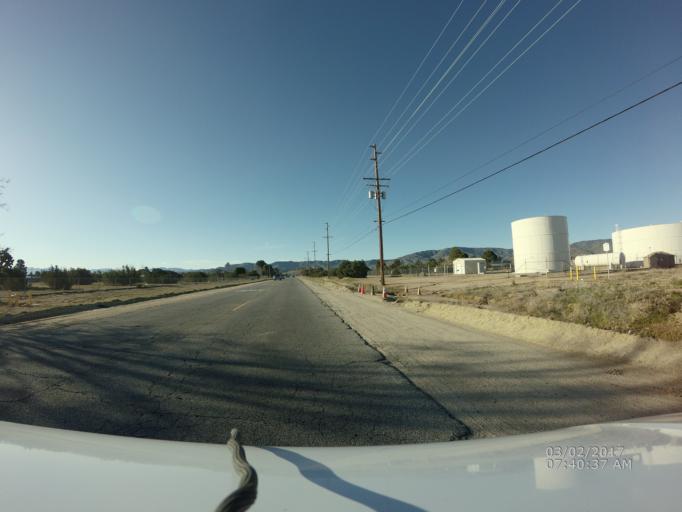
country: US
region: California
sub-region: Los Angeles County
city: Desert View Highlands
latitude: 34.6144
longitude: -118.1655
